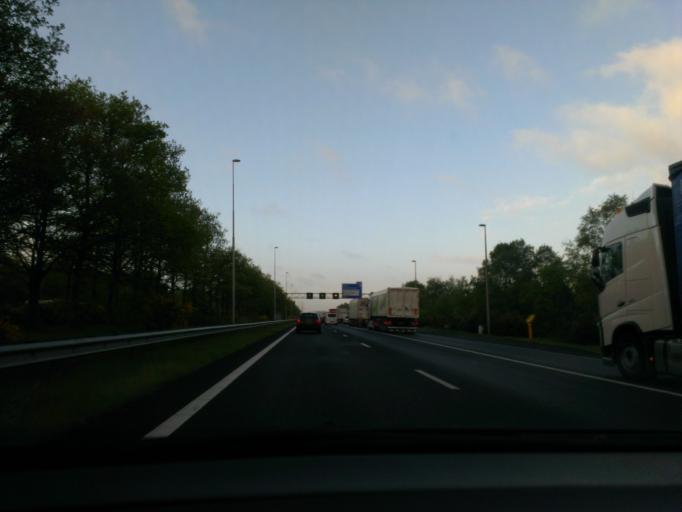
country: NL
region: Gelderland
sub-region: Gemeente Rozendaal
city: Rozendaal
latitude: 52.0468
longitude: 5.9350
